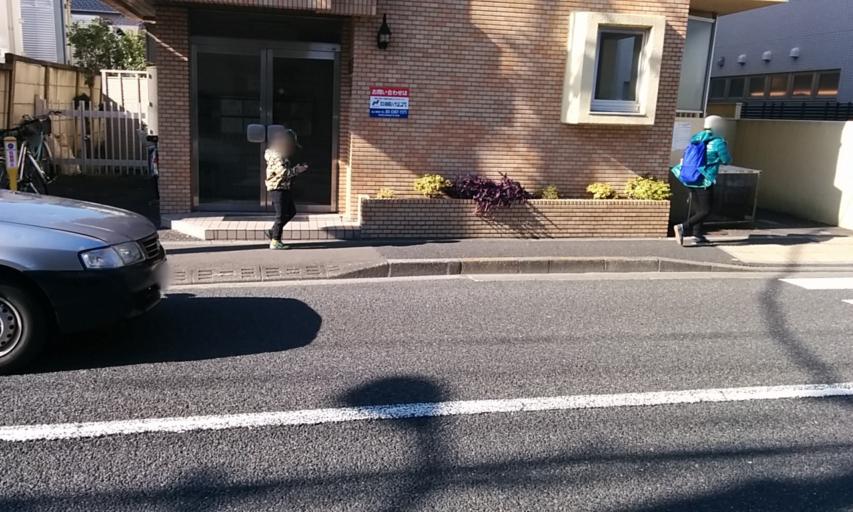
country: JP
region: Tokyo
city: Mitaka-shi
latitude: 35.6650
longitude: 139.5830
